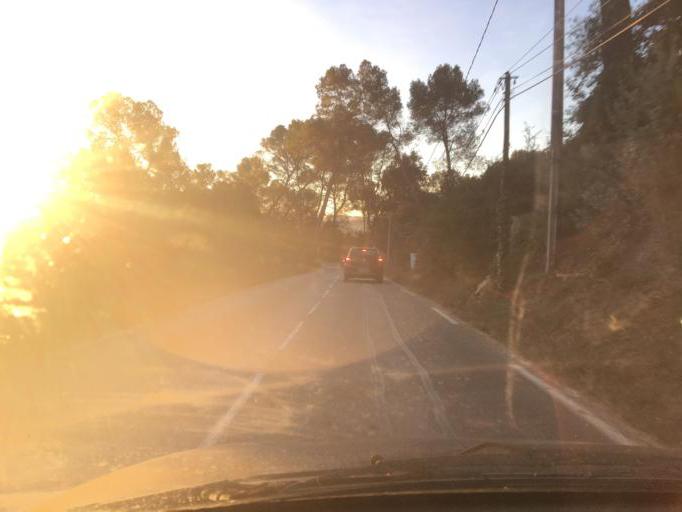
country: FR
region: Provence-Alpes-Cote d'Azur
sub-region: Departement du Var
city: Taradeau
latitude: 43.4552
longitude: 6.4221
